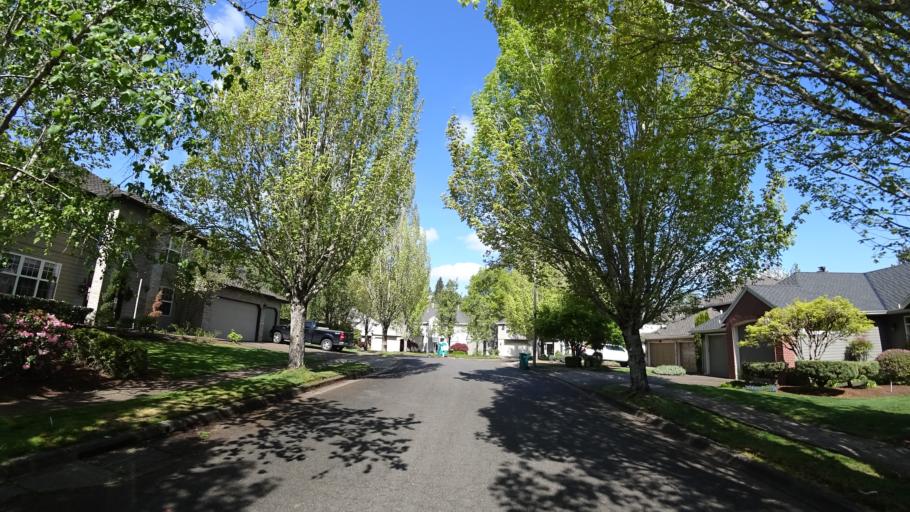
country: US
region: Oregon
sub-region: Washington County
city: King City
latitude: 45.4383
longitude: -122.8371
